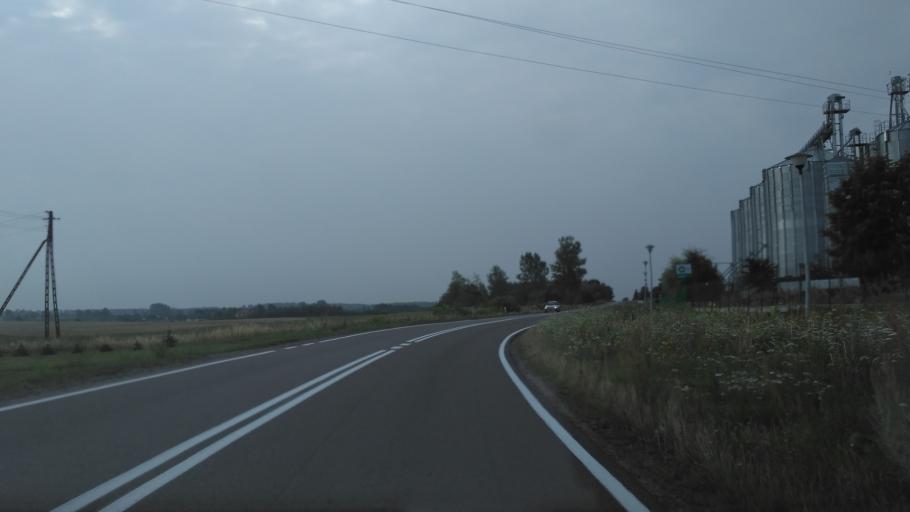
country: PL
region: Lublin Voivodeship
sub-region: Powiat chelmski
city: Rejowiec Fabryczny
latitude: 51.1840
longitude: 23.1735
